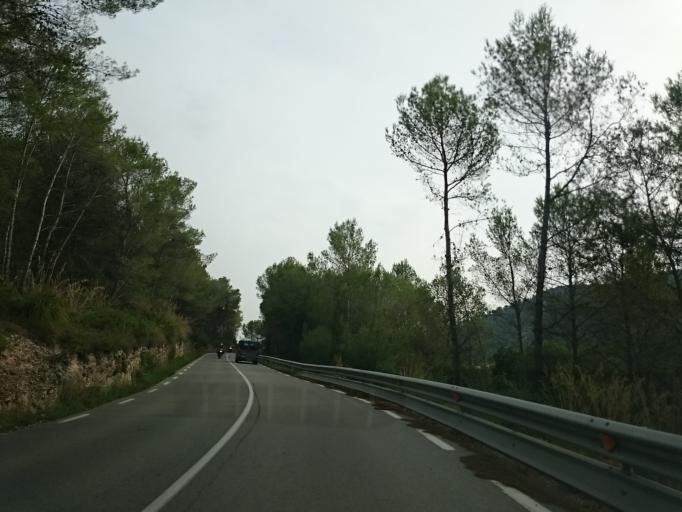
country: ES
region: Catalonia
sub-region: Provincia de Barcelona
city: Sant Pere de Ribes
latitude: 41.2844
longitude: 1.7769
